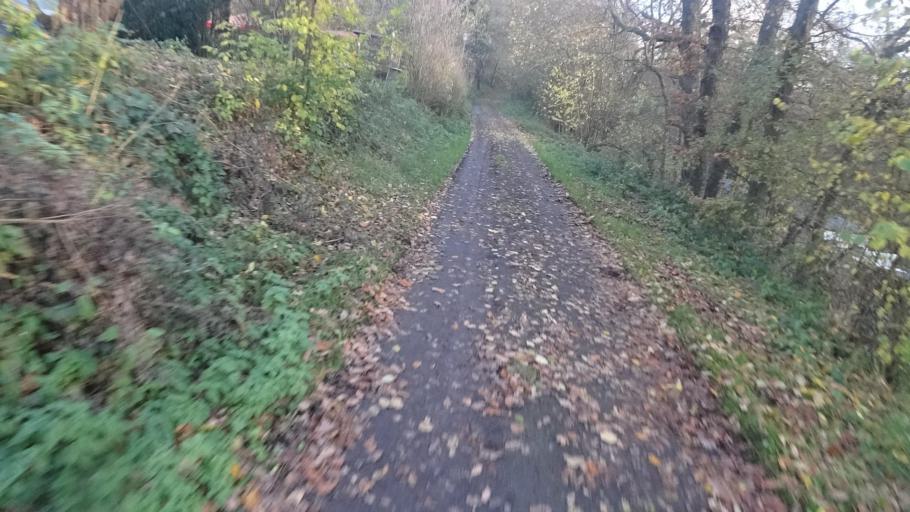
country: DE
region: Rheinland-Pfalz
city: Hausbay
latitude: 50.1062
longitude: 7.5620
